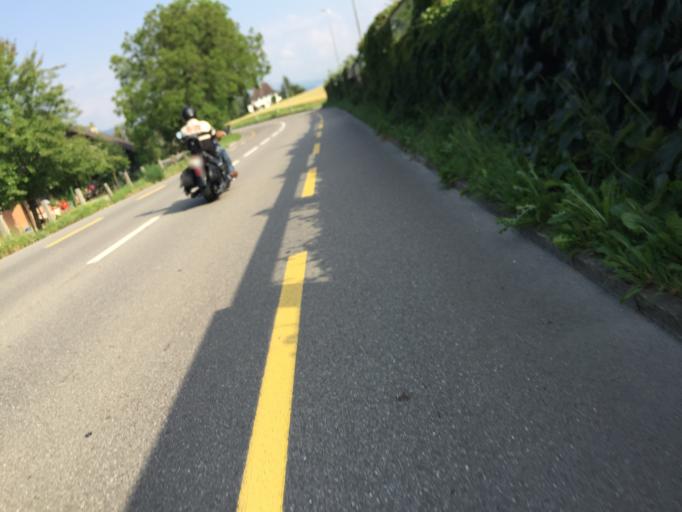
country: CH
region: Bern
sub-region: Bern-Mittelland District
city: Rubigen
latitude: 46.9139
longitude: 7.5253
